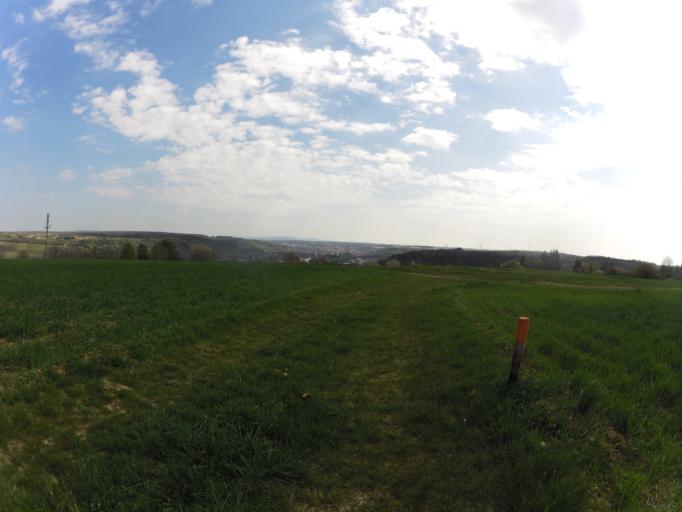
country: DE
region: Bavaria
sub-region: Regierungsbezirk Unterfranken
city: Sommerhausen
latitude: 49.6819
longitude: 10.0184
